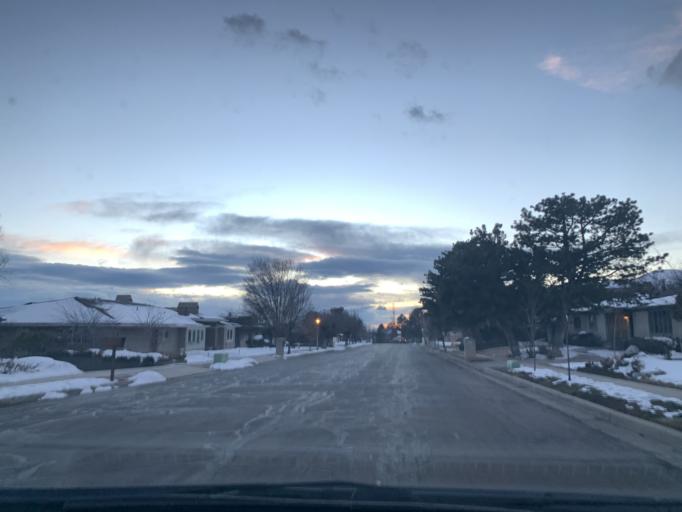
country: US
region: Utah
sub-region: Salt Lake County
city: Salt Lake City
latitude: 40.7813
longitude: -111.8509
